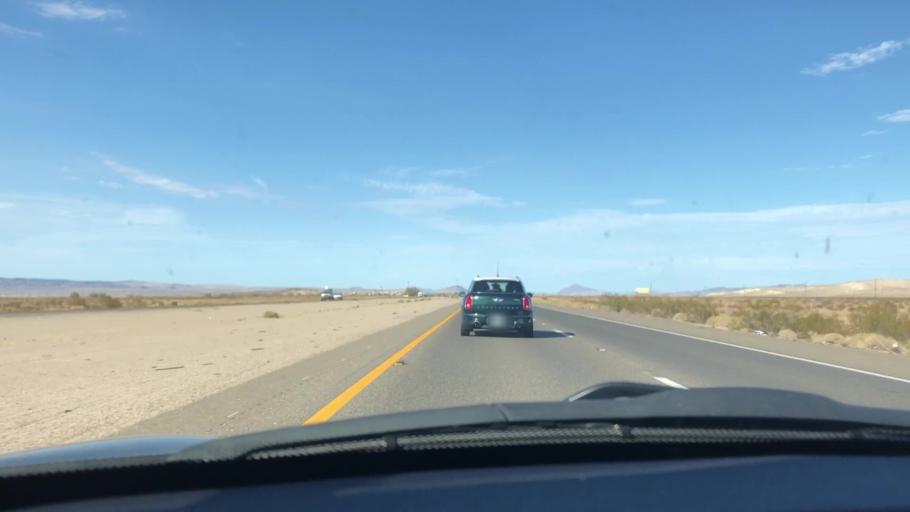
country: US
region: California
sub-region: San Bernardino County
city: Barstow
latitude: 34.9367
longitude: -116.7046
